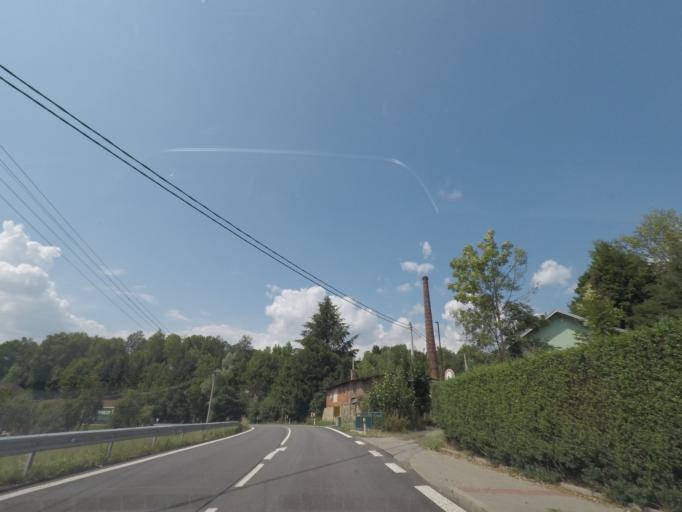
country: CZ
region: Kralovehradecky
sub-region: Okres Trutnov
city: Hostinne
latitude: 50.5228
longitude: 15.7626
